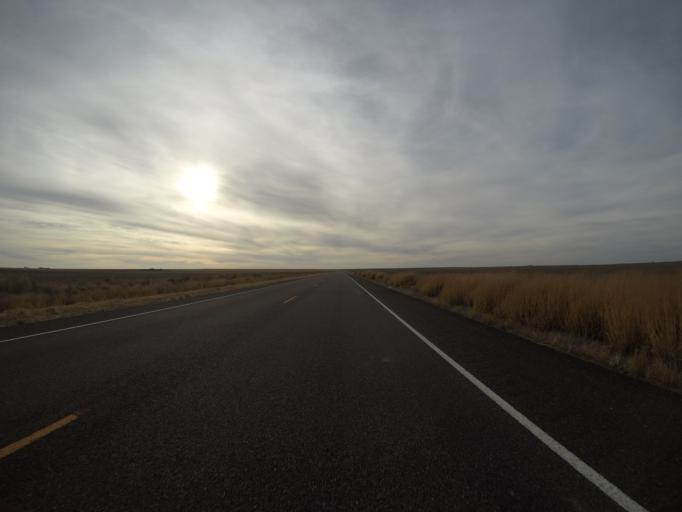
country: US
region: Kansas
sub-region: Cheyenne County
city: Saint Francis
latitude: 39.7462
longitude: -102.1142
